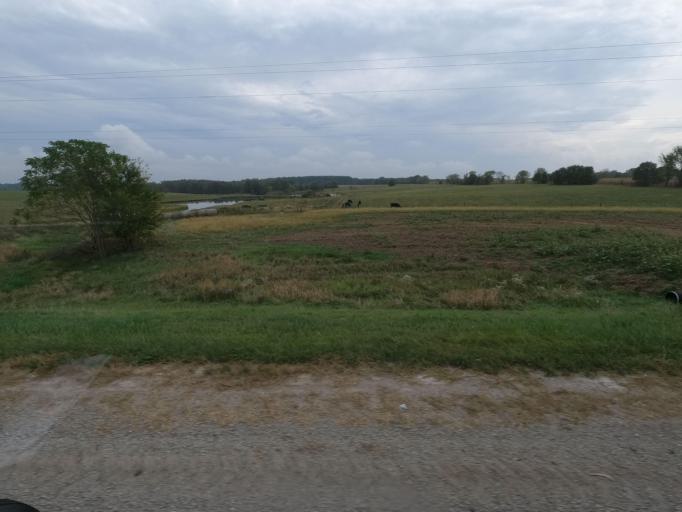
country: US
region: Iowa
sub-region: Van Buren County
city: Keosauqua
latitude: 40.8503
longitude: -92.0436
